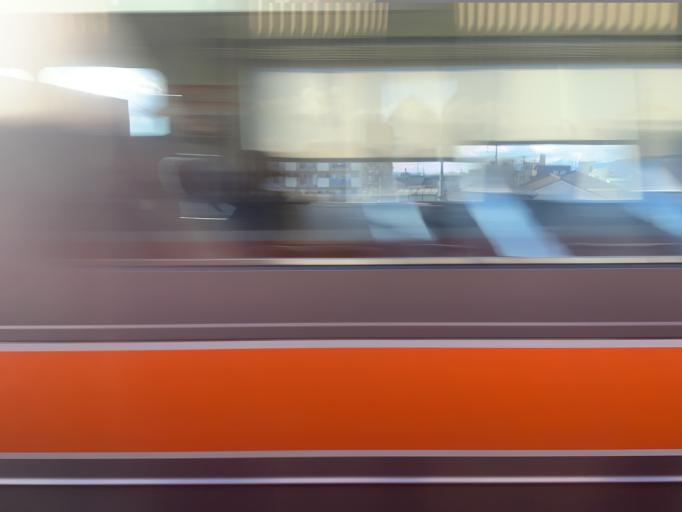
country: JP
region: Gifu
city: Gifu-shi
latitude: 35.3999
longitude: 136.7722
